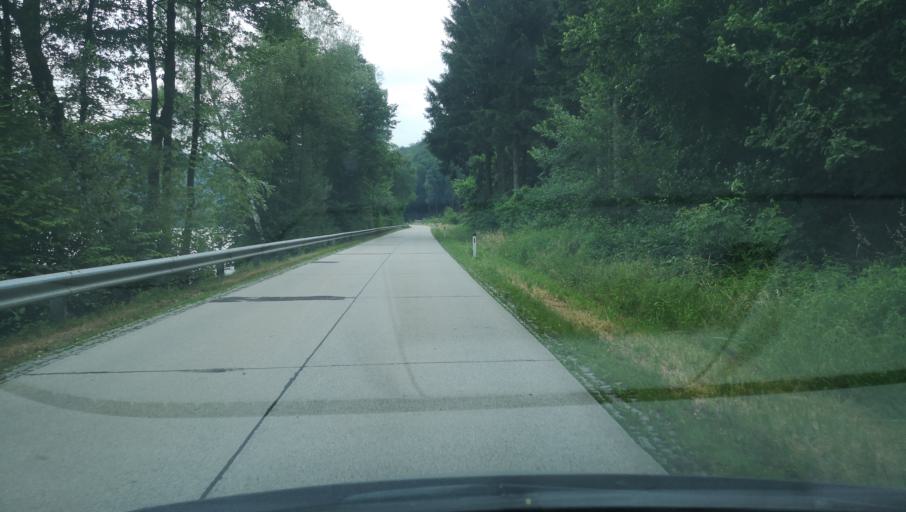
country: AT
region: Lower Austria
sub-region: Politischer Bezirk Melk
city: Nochling
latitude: 48.1932
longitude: 15.0308
